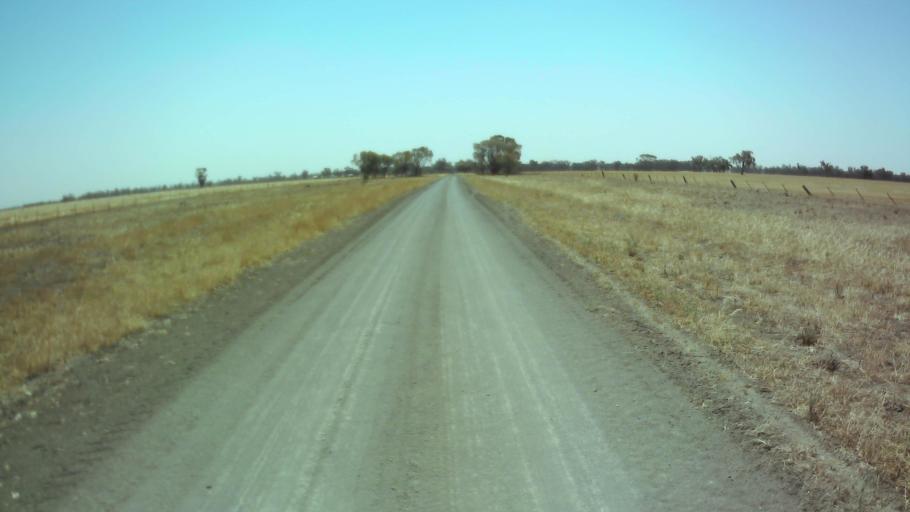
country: AU
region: New South Wales
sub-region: Weddin
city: Grenfell
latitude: -33.9913
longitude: 147.8635
